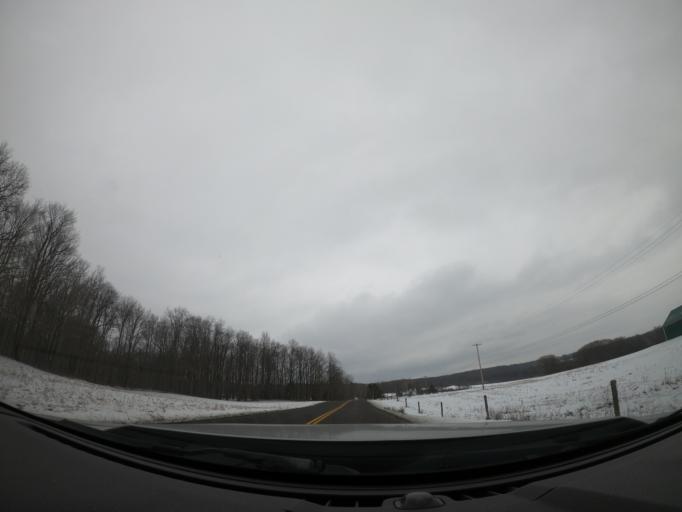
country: US
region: New York
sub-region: Cayuga County
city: Moravia
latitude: 42.7510
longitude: -76.3679
